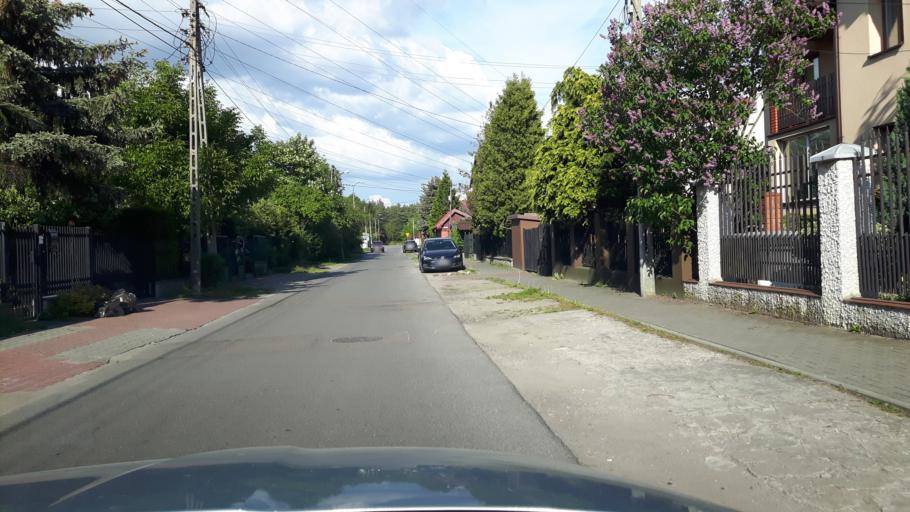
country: PL
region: Masovian Voivodeship
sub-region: Warszawa
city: Rembertow
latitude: 52.2512
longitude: 21.1270
